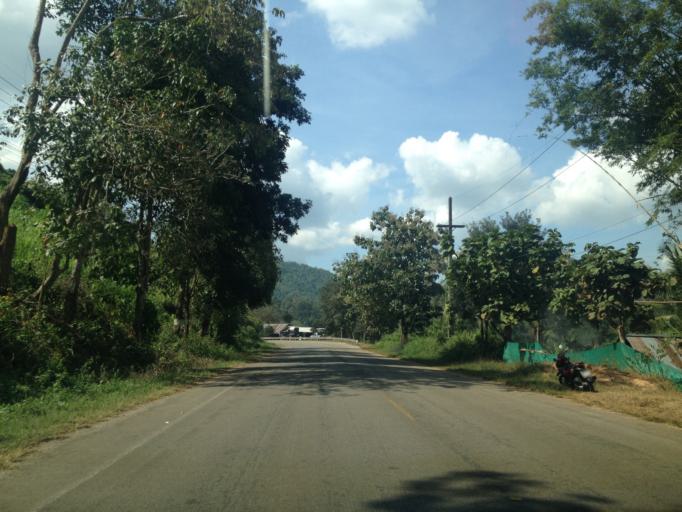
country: TH
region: Chiang Mai
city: Samoeng
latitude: 18.8079
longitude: 98.8251
